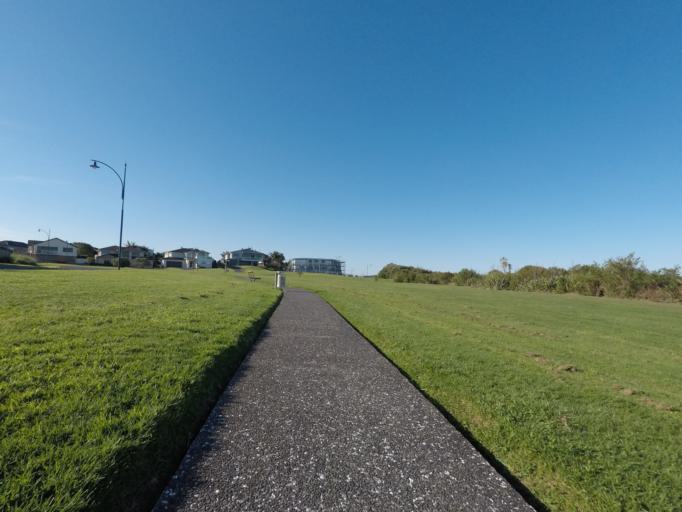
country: NZ
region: Auckland
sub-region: Auckland
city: Rosebank
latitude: -36.8372
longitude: 174.6613
